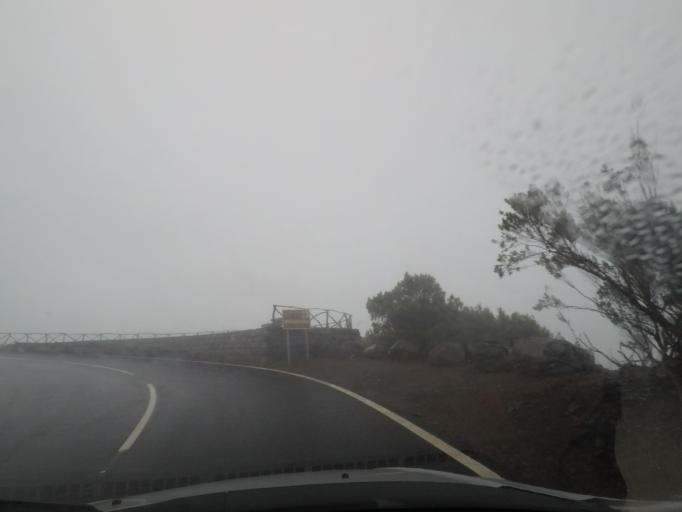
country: PT
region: Madeira
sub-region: Santana
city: Santana
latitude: 32.7708
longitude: -16.9172
